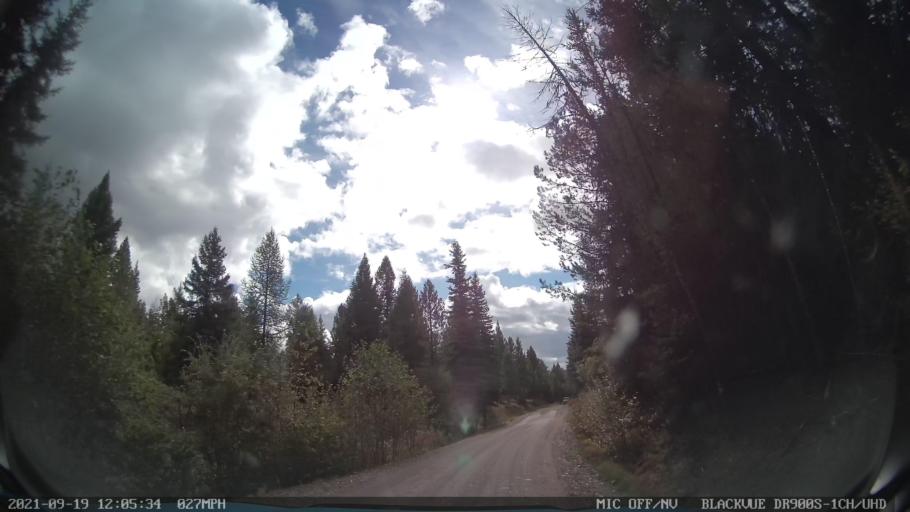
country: US
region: Montana
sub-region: Missoula County
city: Seeley Lake
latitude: 47.1907
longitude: -113.4243
